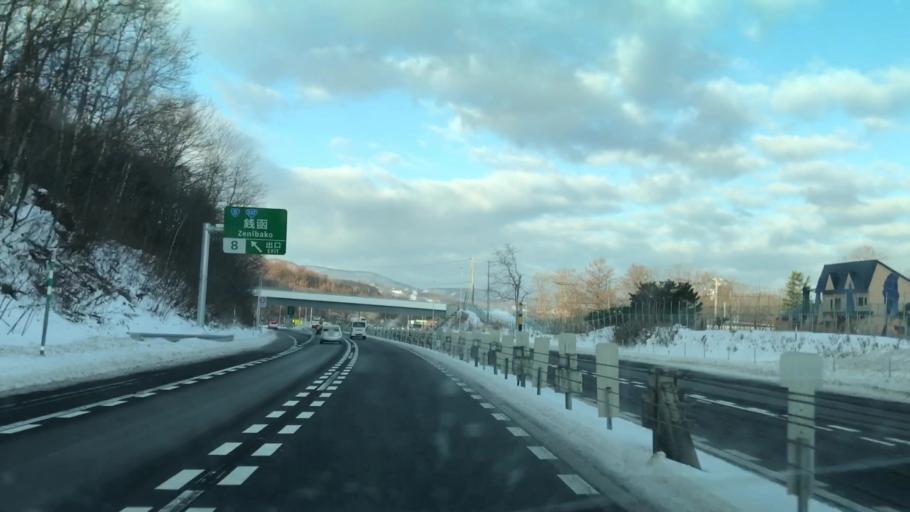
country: JP
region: Hokkaido
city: Sapporo
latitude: 43.1325
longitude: 141.1793
